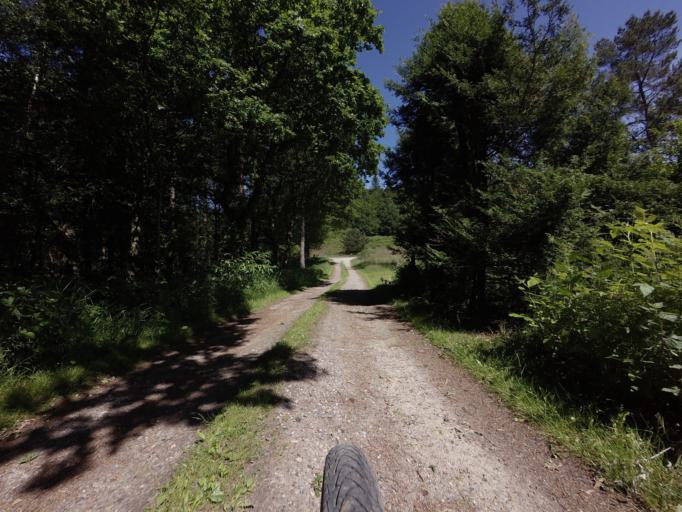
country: DK
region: Central Jutland
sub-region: Silkeborg Kommune
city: Virklund
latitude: 56.0634
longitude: 9.4736
